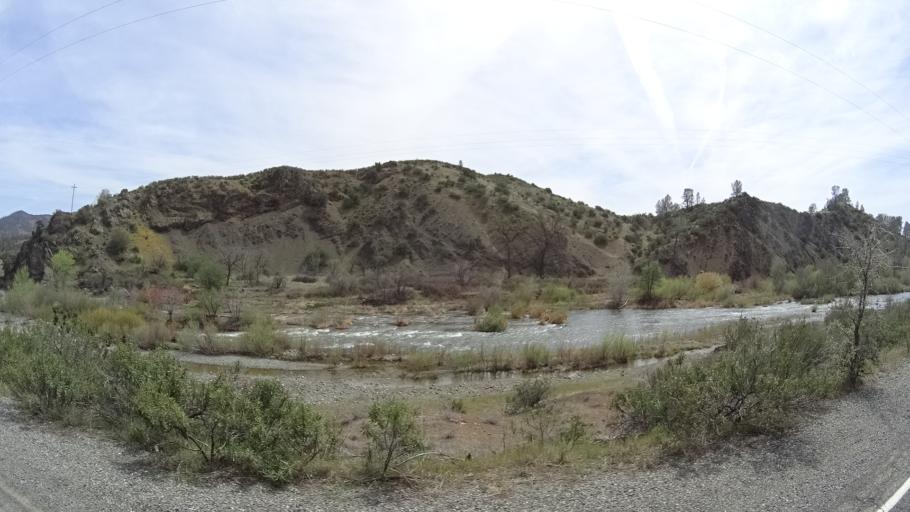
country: US
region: California
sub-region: Glenn County
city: Willows
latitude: 39.4272
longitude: -122.5139
